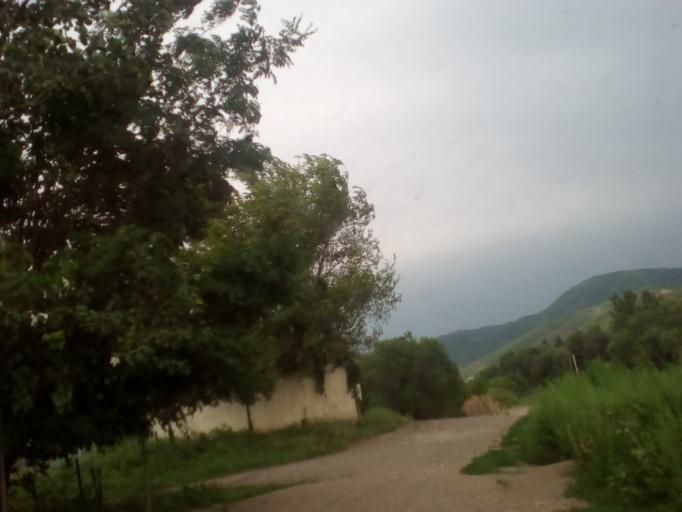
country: KZ
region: Almaty Oblysy
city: Burunday
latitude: 43.1576
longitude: 76.4012
